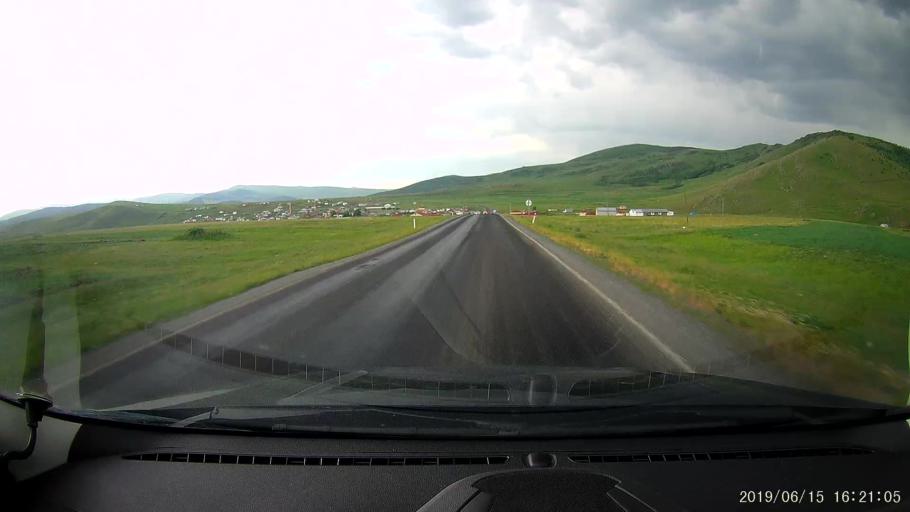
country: TR
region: Ardahan
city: Hanak
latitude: 41.2030
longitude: 42.8462
